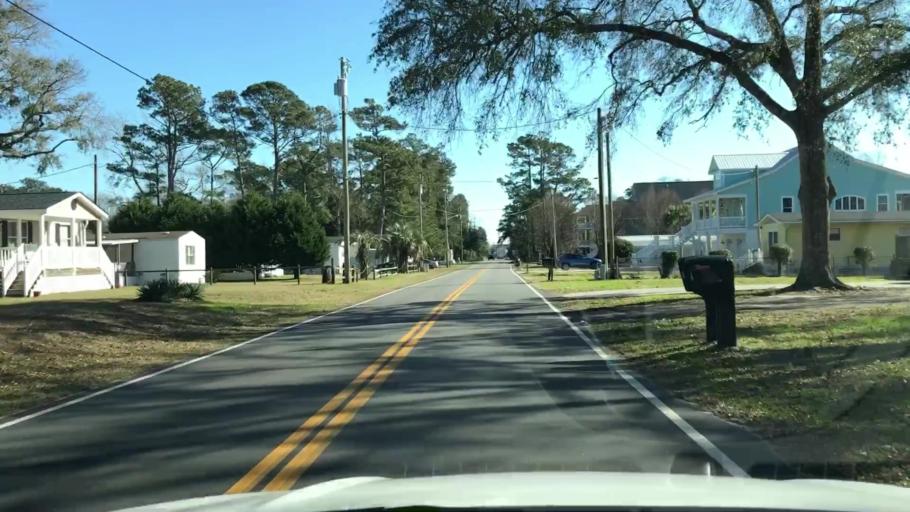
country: US
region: South Carolina
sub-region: Horry County
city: Garden City
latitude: 33.5904
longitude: -78.9969
